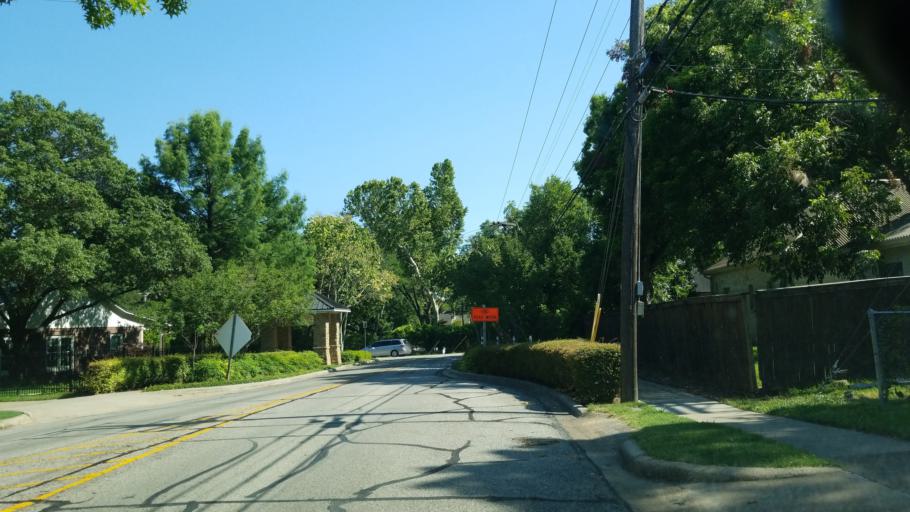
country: US
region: Texas
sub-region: Dallas County
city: Farmers Branch
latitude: 32.9184
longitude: -96.8876
